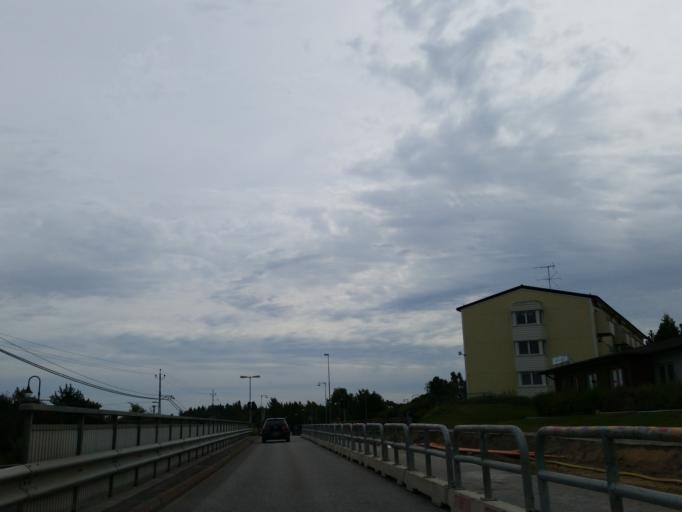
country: SE
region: Stockholm
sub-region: Nykvarns Kommun
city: Nykvarn
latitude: 59.1780
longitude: 17.4331
